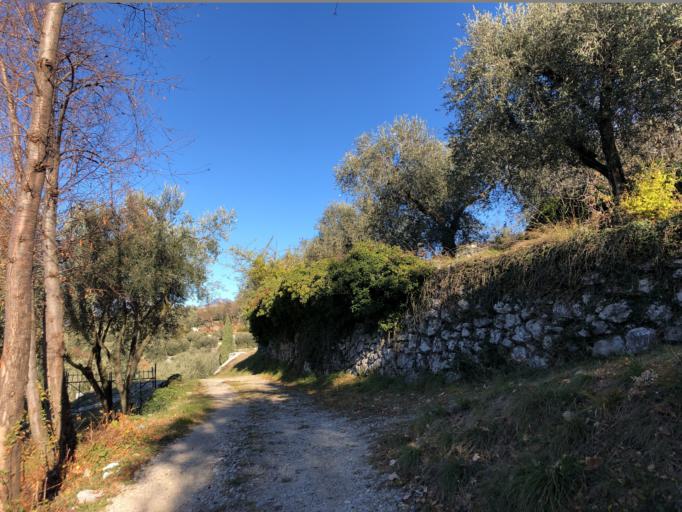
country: IT
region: Trentino-Alto Adige
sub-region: Provincia di Trento
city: Torbole sul Garda
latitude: 45.8671
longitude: 10.8851
